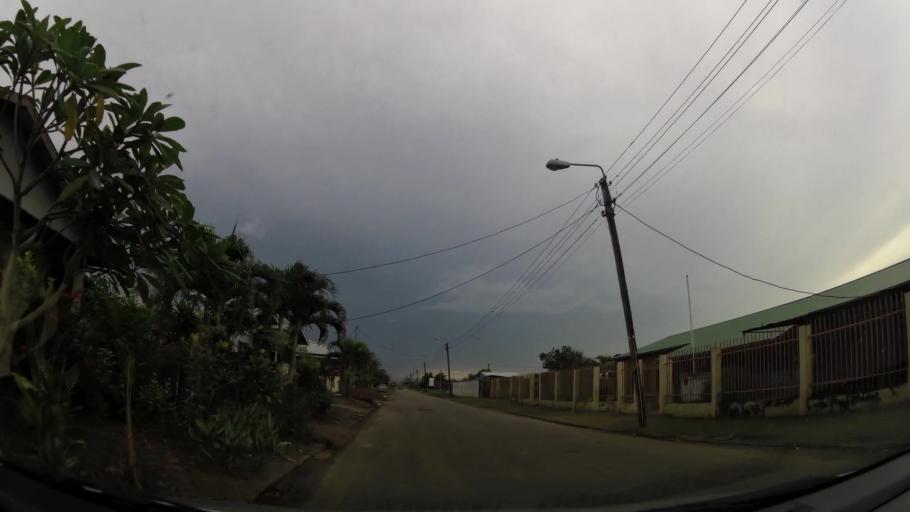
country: SR
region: Paramaribo
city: Paramaribo
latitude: 5.8093
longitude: -55.1964
